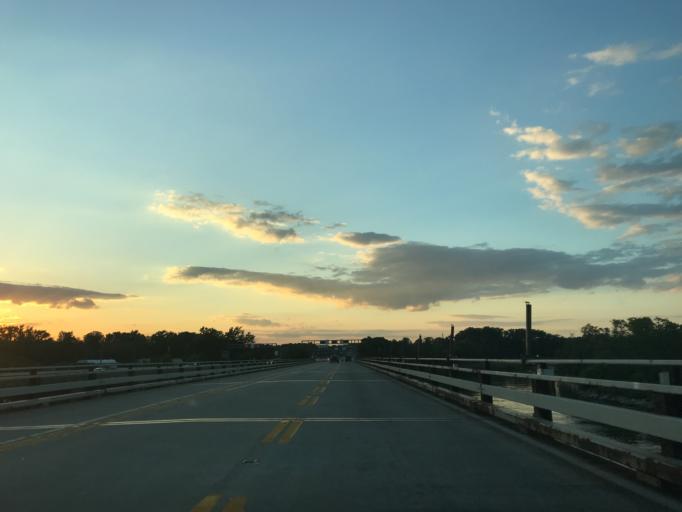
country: US
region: Maryland
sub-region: Anne Arundel County
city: Cape Saint Claire
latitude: 39.0069
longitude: -76.4027
